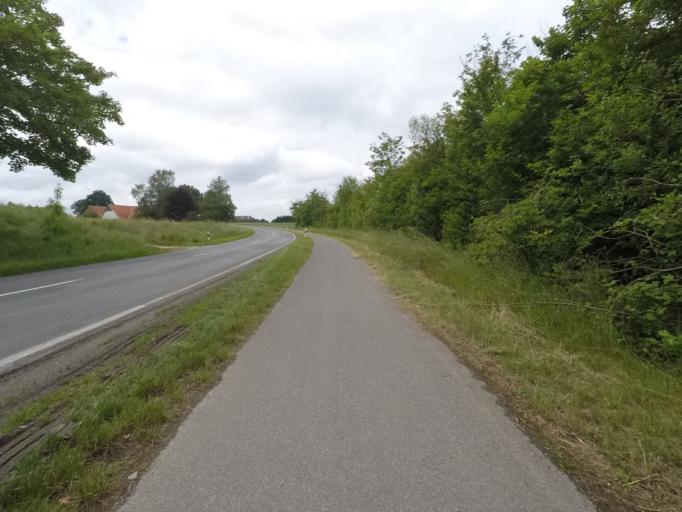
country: DE
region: North Rhine-Westphalia
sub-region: Regierungsbezirk Detmold
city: Werther
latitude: 52.1050
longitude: 8.4180
